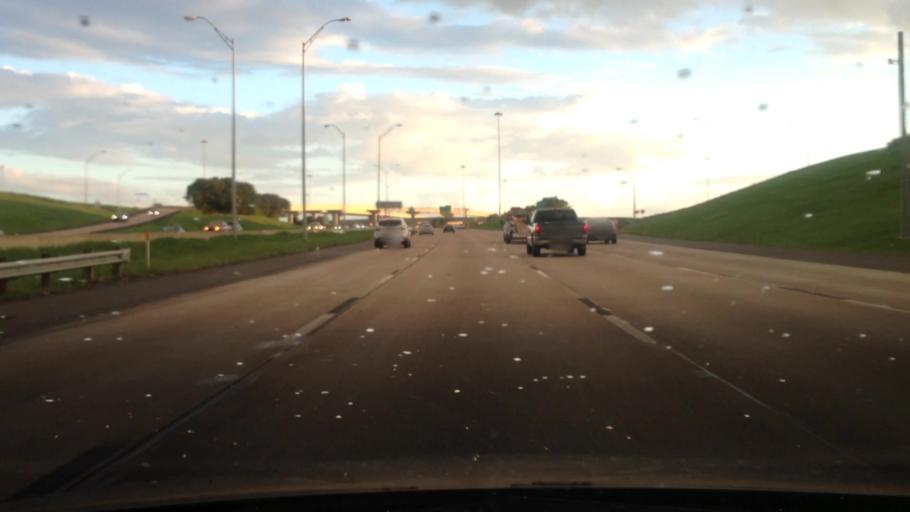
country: US
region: Texas
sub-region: Tarrant County
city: White Settlement
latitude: 32.7440
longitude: -97.4812
